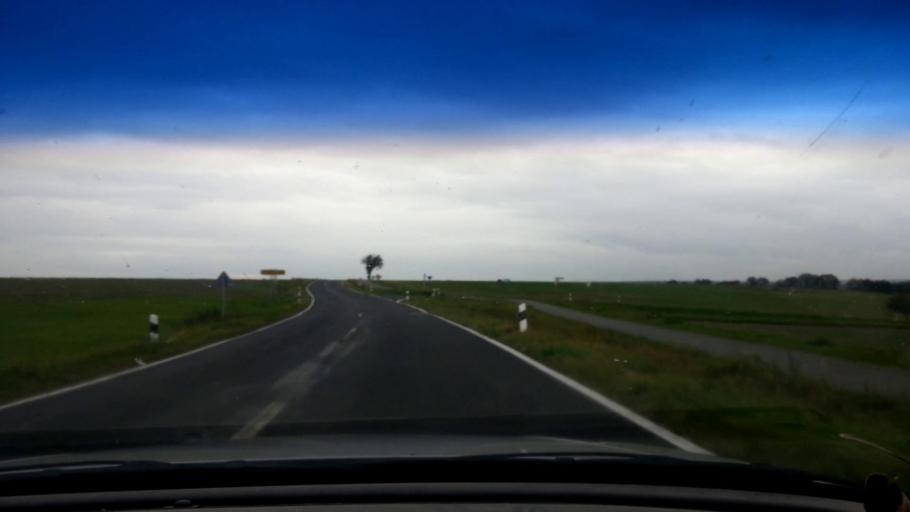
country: DE
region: Bavaria
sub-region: Upper Franconia
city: Priesendorf
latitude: 49.8833
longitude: 10.6480
